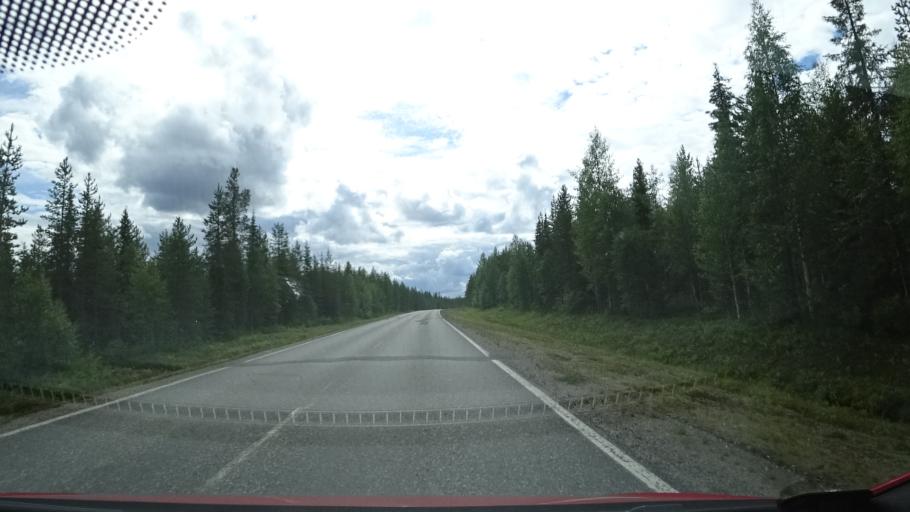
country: FI
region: Lapland
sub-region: Tunturi-Lappi
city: Kittilae
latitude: 67.5245
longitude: 24.9081
